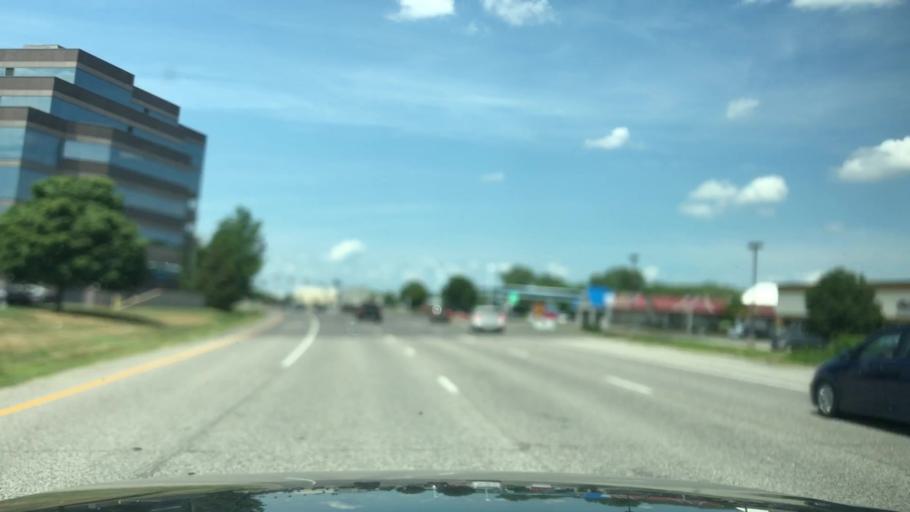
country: US
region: Missouri
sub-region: Saint Charles County
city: Saint Charles
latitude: 38.7608
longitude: -90.4558
